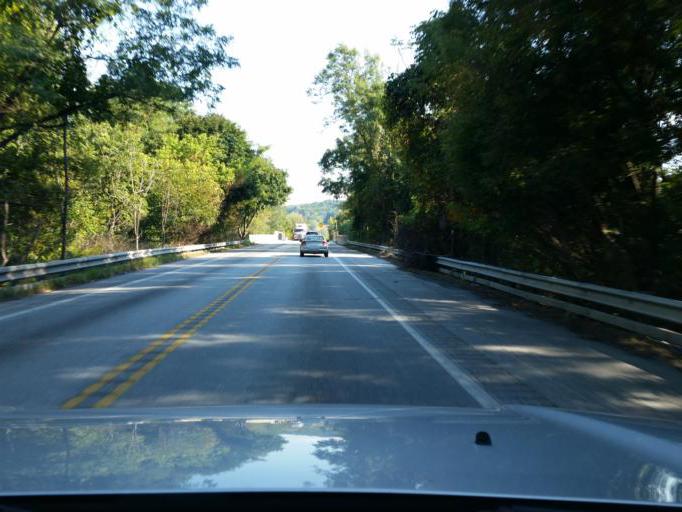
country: US
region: Pennsylvania
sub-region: Chester County
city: Atglen
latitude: 39.9521
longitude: -75.9720
